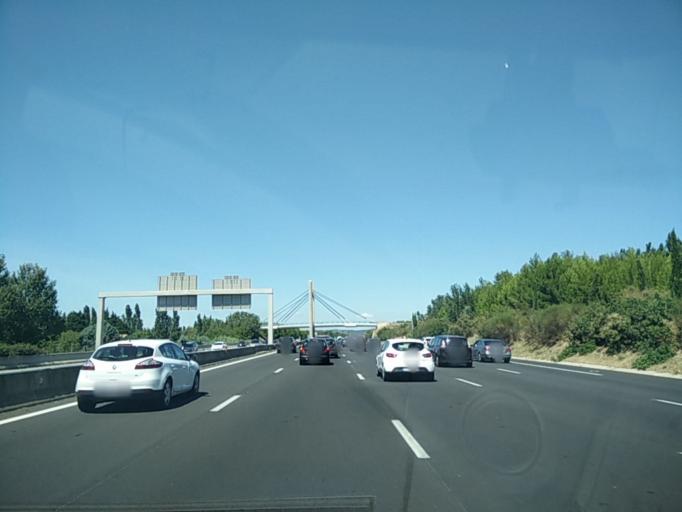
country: FR
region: Provence-Alpes-Cote d'Azur
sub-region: Departement du Vaucluse
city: Orange
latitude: 44.1424
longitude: 4.7781
